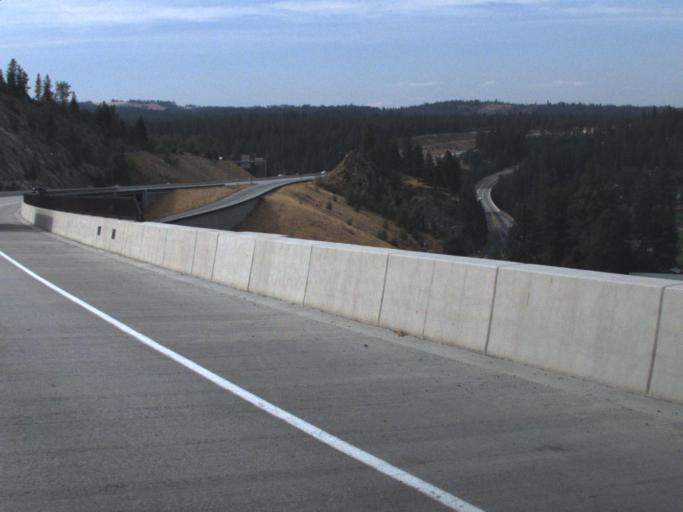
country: US
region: Washington
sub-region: Spokane County
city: Fairwood
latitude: 47.7795
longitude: -117.3999
